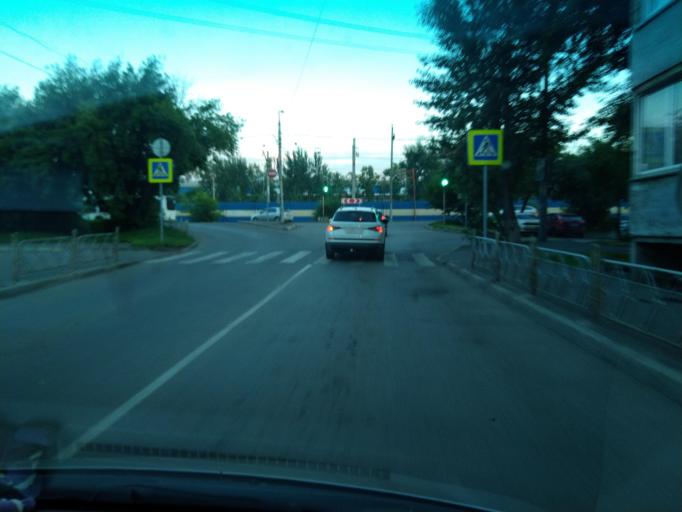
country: RU
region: Krasnoyarskiy
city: Krasnoyarsk
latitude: 55.9835
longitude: 92.8716
